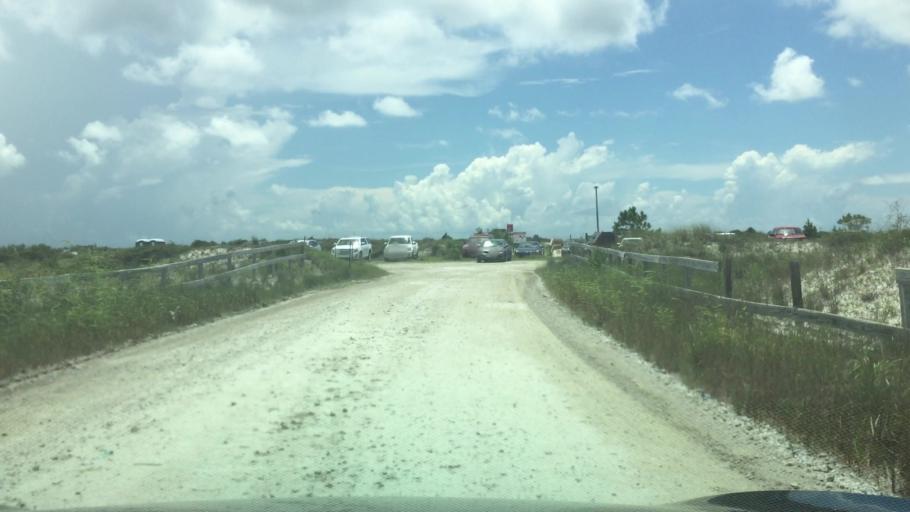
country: US
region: Florida
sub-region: Bay County
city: Mexico Beach
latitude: 29.9594
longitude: -85.4569
